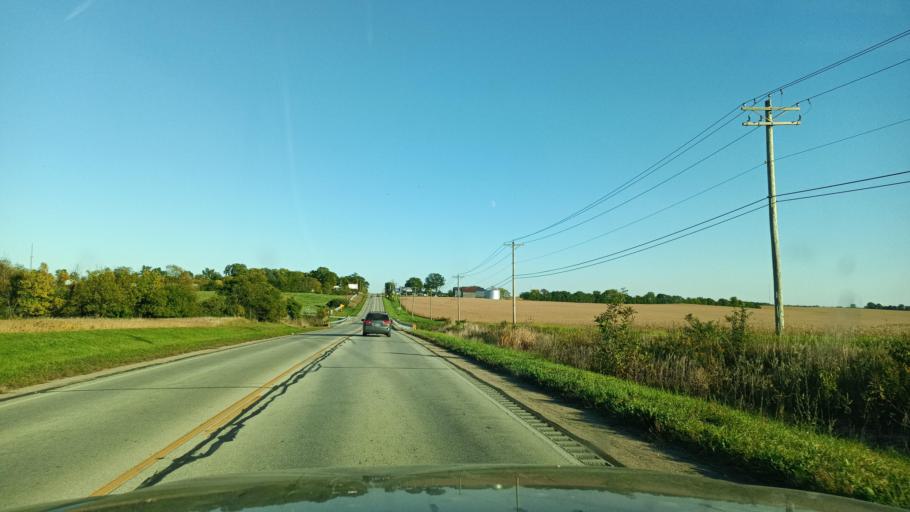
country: US
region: Illinois
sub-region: Champaign County
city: Lake of the Woods
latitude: 40.1587
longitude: -88.3118
